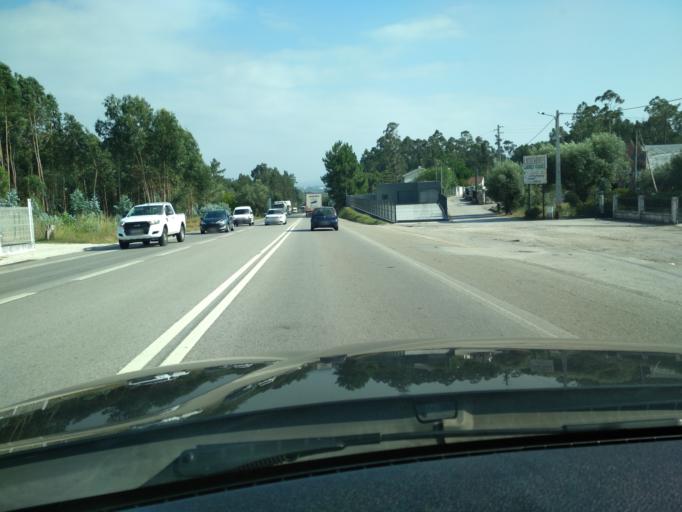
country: PT
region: Aveiro
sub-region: Mealhada
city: Pampilhosa do Botao
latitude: 40.3014
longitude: -8.4470
